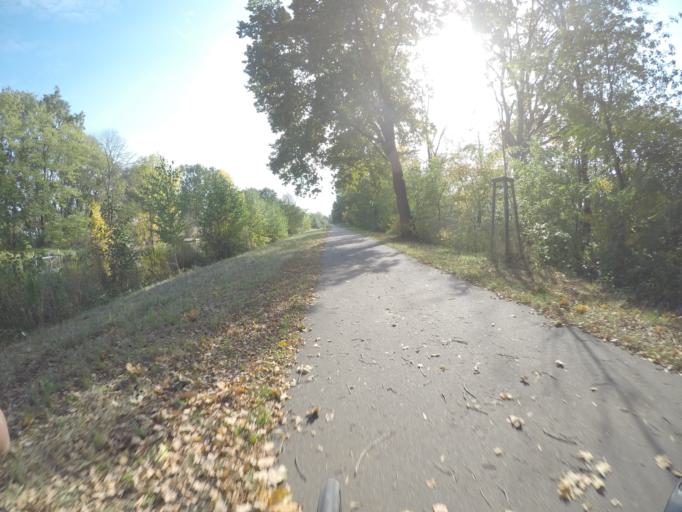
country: DE
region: Brandenburg
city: Oranienburg
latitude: 52.7215
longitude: 13.2341
